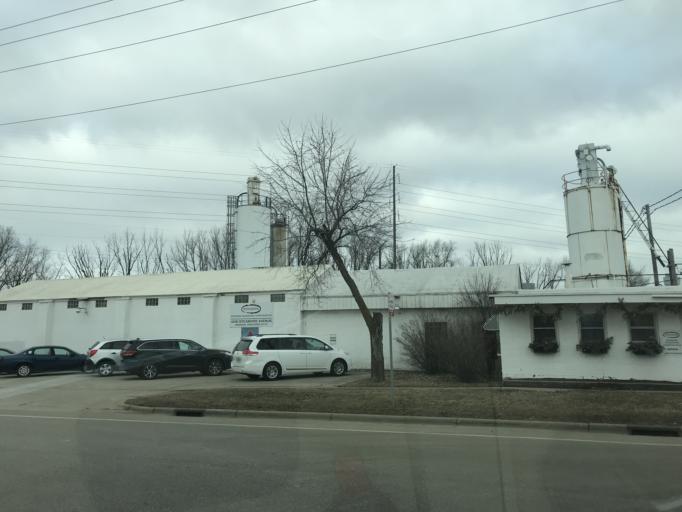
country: US
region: Wisconsin
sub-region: Dane County
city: Monona
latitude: 43.1137
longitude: -89.3094
